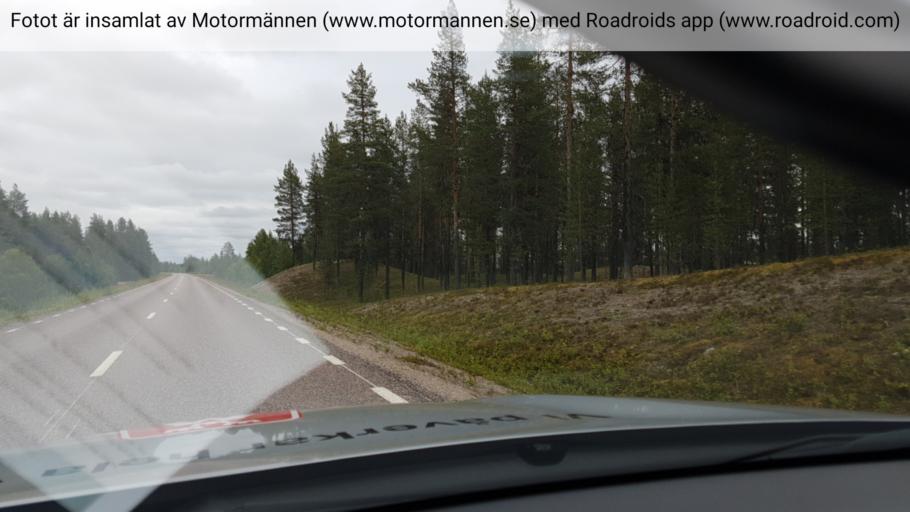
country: SE
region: Norrbotten
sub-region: Gallivare Kommun
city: Gaellivare
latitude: 67.0755
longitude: 21.3574
